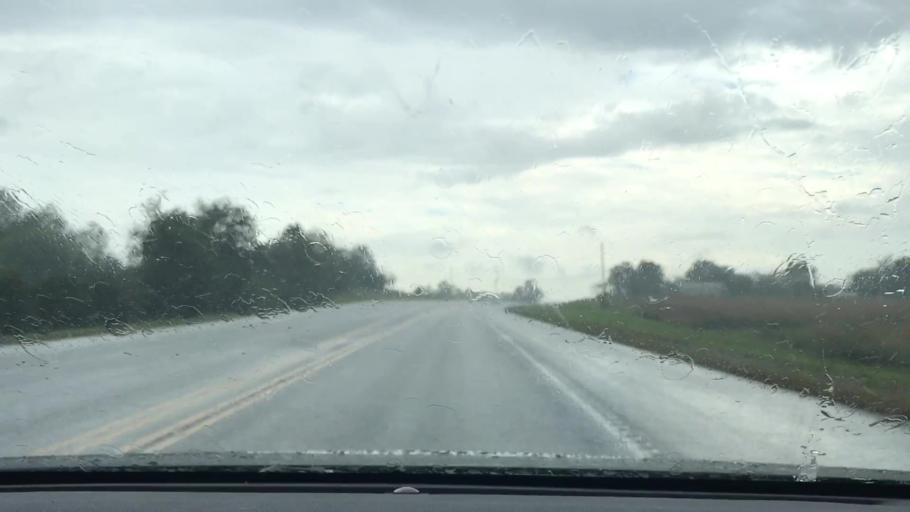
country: US
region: Tennessee
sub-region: Macon County
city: Lafayette
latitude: 36.5003
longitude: -85.9618
